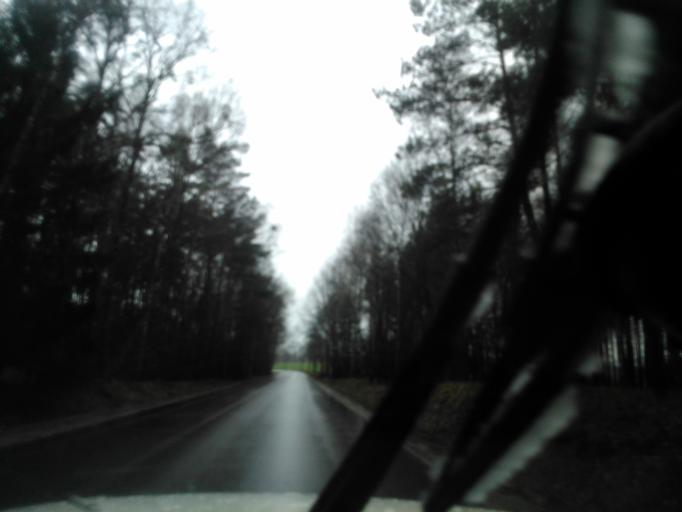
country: PL
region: Warmian-Masurian Voivodeship
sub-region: Powiat dzialdowski
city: Rybno
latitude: 53.3235
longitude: 19.9054
